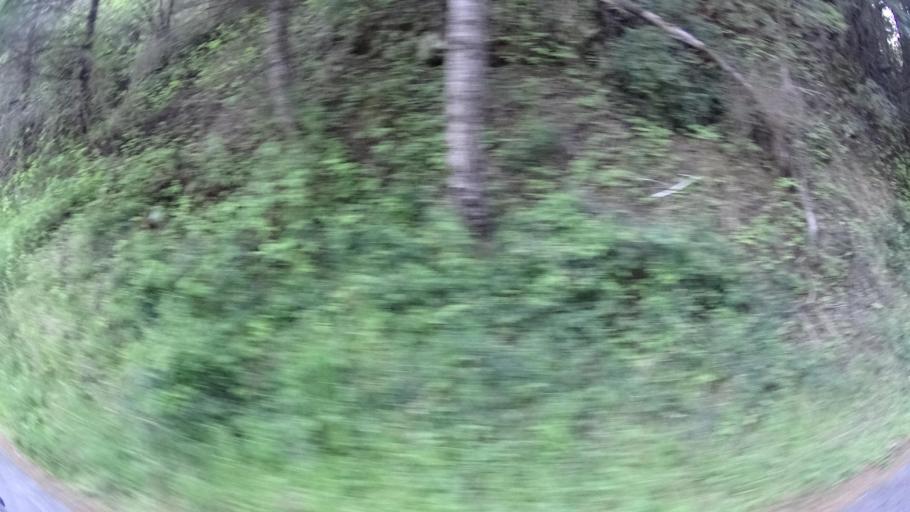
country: US
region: California
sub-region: Humboldt County
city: Rio Dell
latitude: 40.4515
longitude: -123.9803
